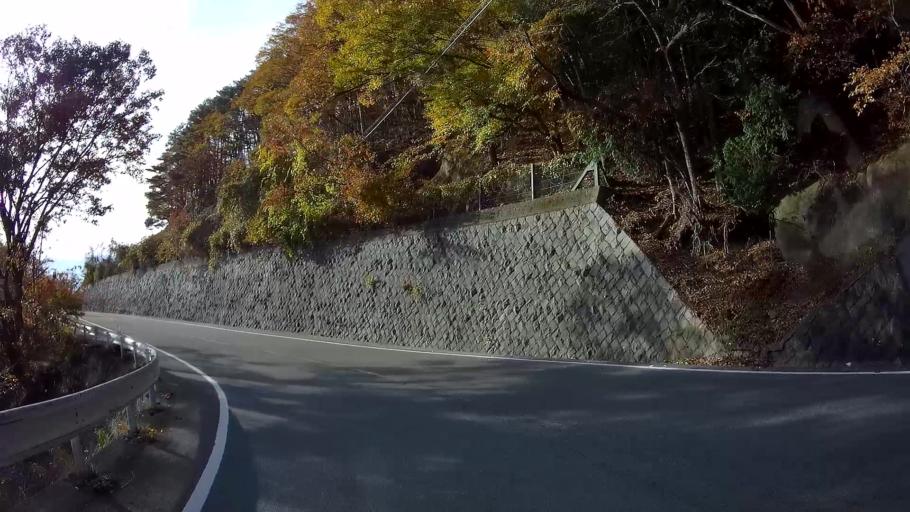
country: JP
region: Yamanashi
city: Fujikawaguchiko
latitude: 35.4779
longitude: 138.5615
